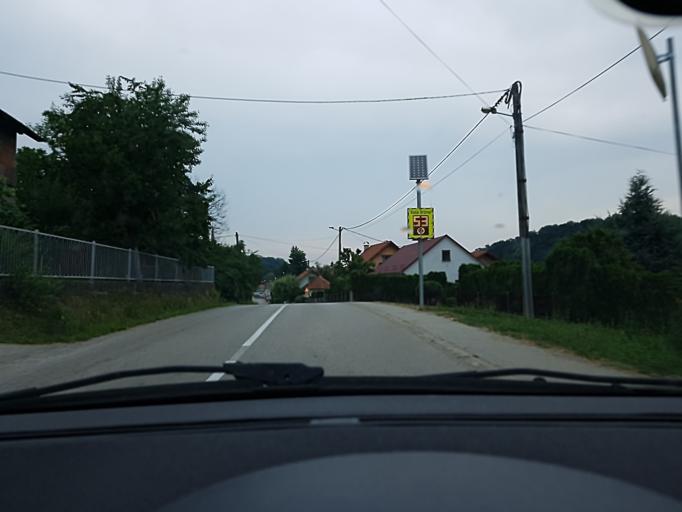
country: HR
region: Zagrebacka
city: Jakovlje
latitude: 45.9576
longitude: 15.8184
